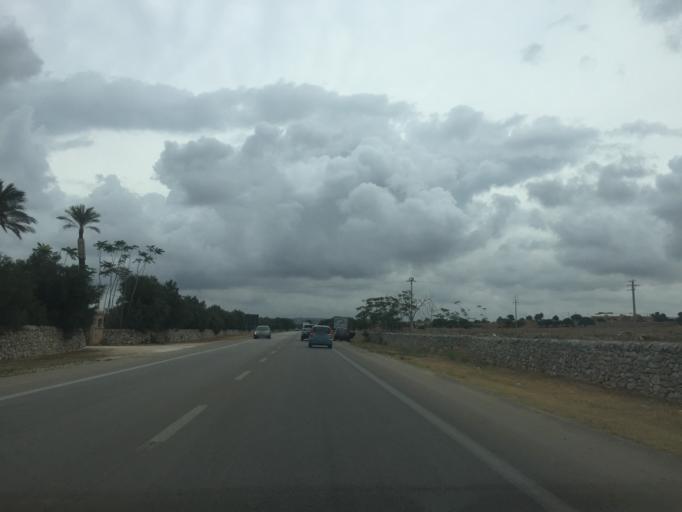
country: IT
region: Sicily
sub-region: Ragusa
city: Marina di Ragusa
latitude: 36.8237
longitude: 14.5820
